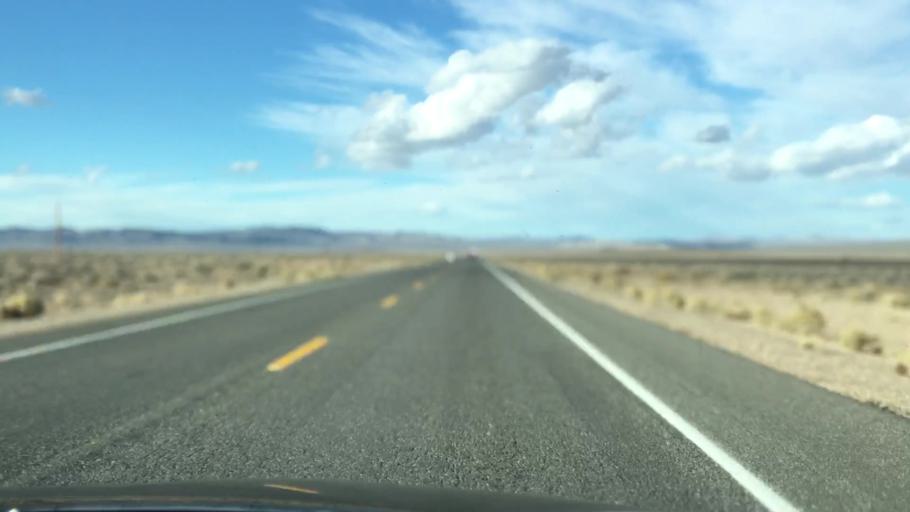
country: US
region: Nevada
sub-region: Esmeralda County
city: Goldfield
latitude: 37.3972
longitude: -117.1474
